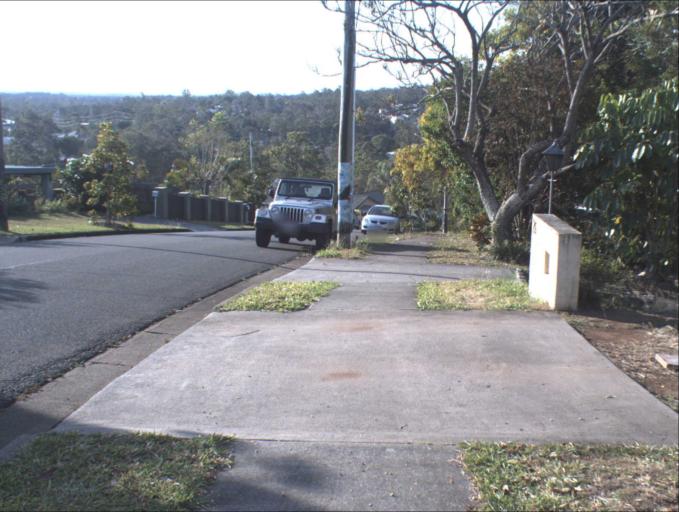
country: AU
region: Queensland
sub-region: Logan
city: Beenleigh
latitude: -27.6735
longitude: 153.2020
